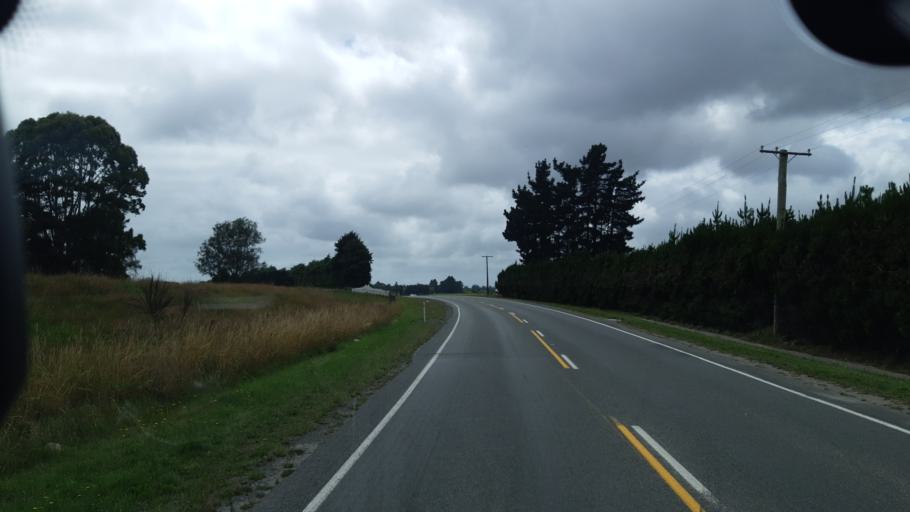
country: NZ
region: Canterbury
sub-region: Christchurch City
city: Christchurch
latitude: -43.4702
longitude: 172.5459
